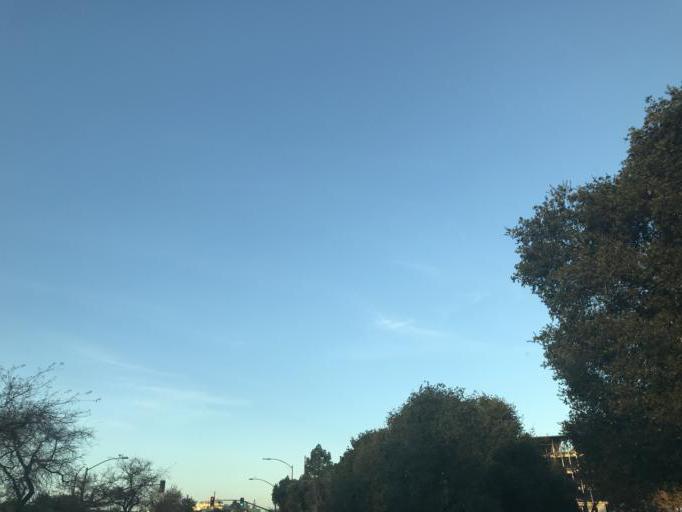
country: US
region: California
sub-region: San Mateo County
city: Menlo Park
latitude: 37.4413
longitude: -122.1705
